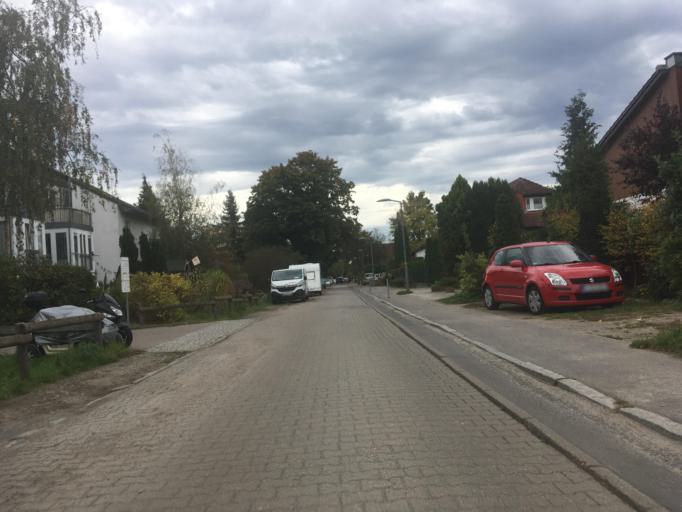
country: DE
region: Berlin
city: Wilhelmstadt
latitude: 52.5162
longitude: 13.1599
